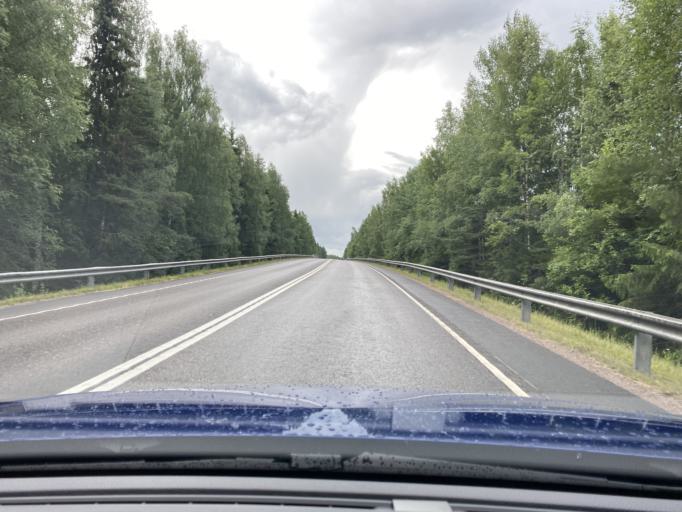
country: FI
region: Uusimaa
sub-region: Helsinki
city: Hyvinge
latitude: 60.5735
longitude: 24.7997
